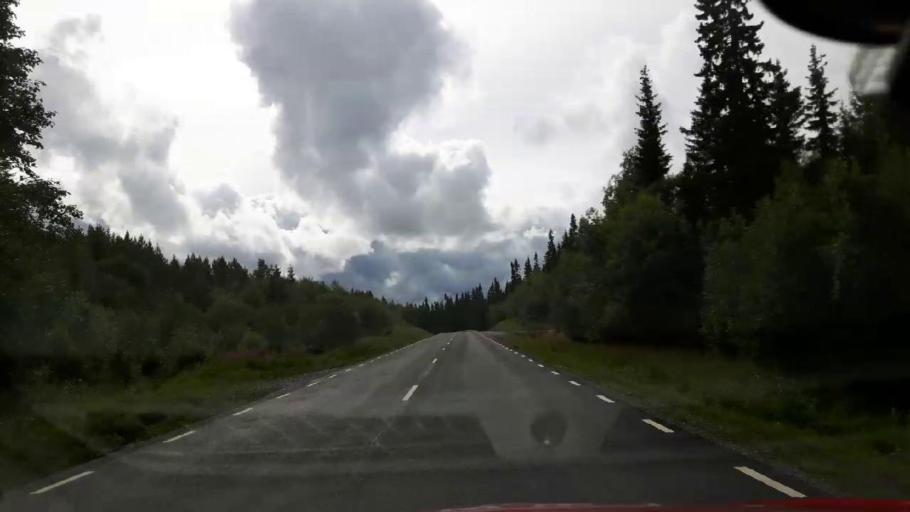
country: NO
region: Nord-Trondelag
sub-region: Lierne
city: Sandvika
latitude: 64.6128
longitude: 14.1200
